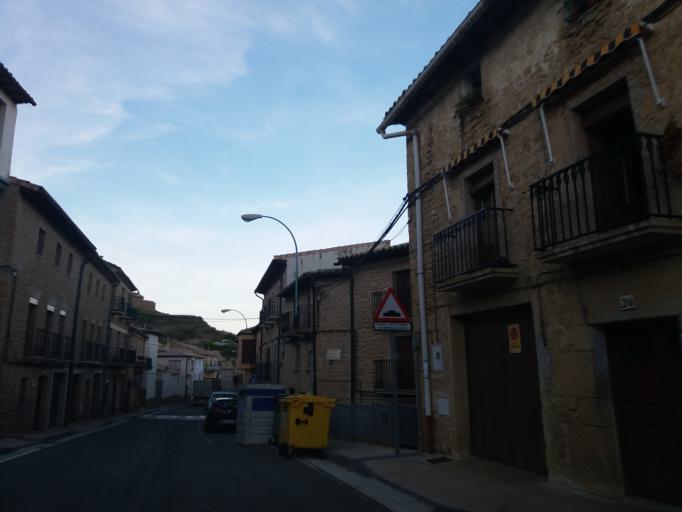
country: ES
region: Navarre
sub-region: Provincia de Navarra
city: San Martin de Unx
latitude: 42.5242
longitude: -1.5604
